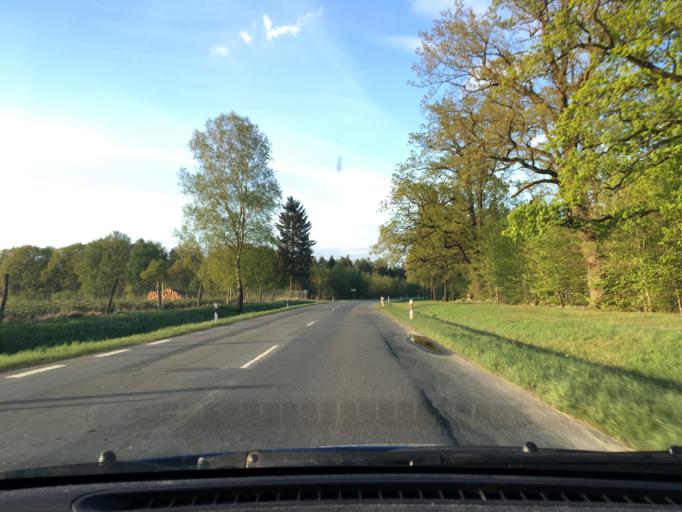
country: DE
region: Lower Saxony
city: Wietzendorf
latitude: 52.9848
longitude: 9.9869
